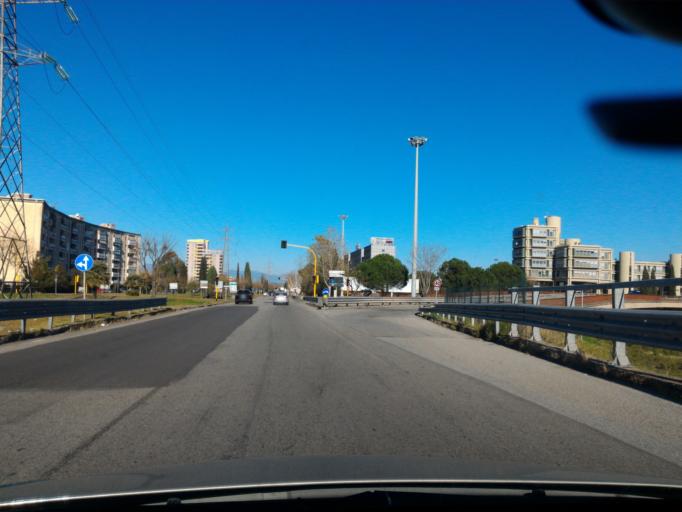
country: IT
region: Calabria
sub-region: Provincia di Cosenza
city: Cosenza
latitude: 39.3171
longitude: 16.2581
